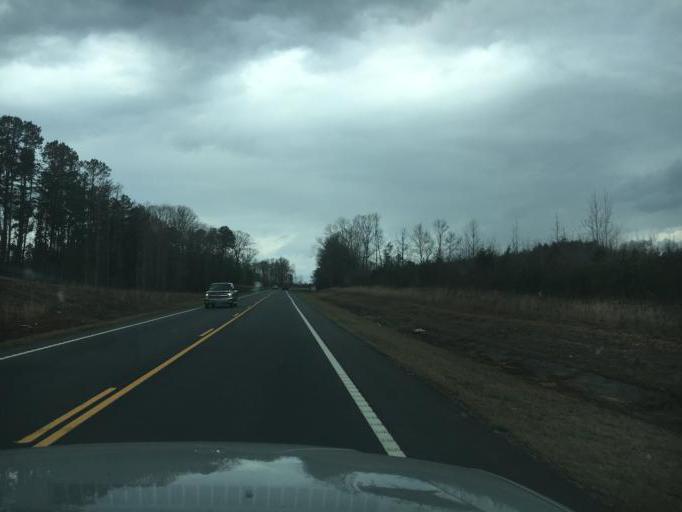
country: US
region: South Carolina
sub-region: Oconee County
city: Walhalla
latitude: 34.7969
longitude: -83.0277
